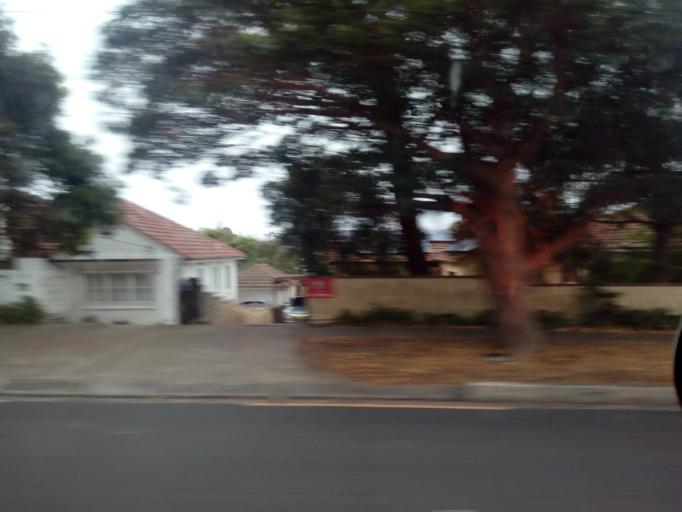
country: AU
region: New South Wales
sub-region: Willoughby
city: Castle Cove
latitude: -33.7959
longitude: 151.2088
